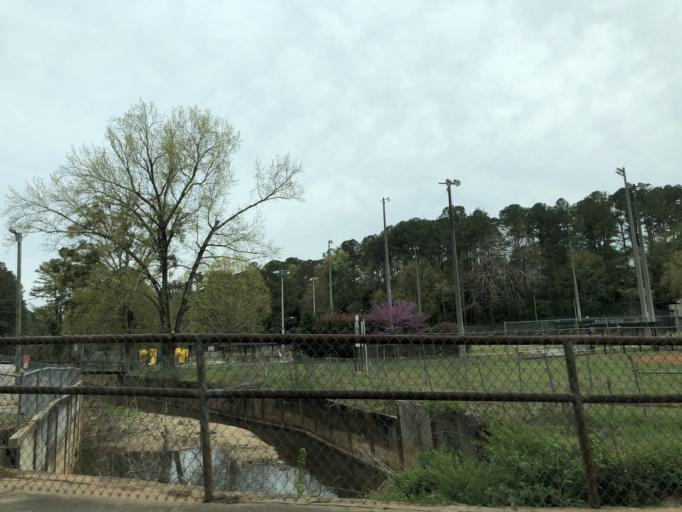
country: US
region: Georgia
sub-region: DeKalb County
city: Belvedere Park
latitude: 33.7548
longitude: -84.2594
